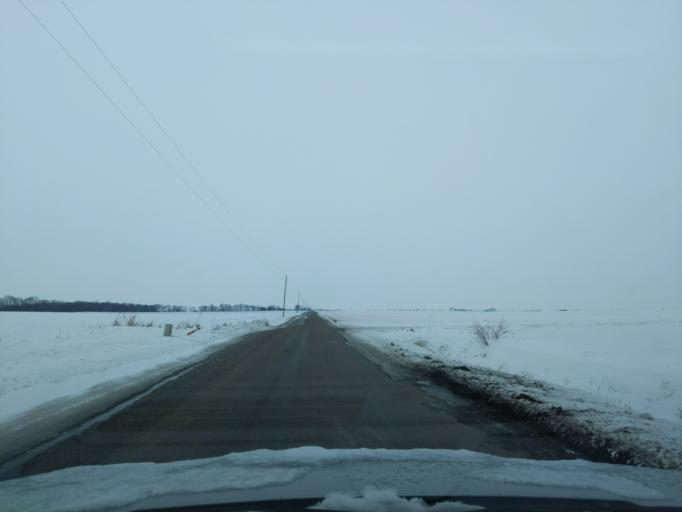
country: US
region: Indiana
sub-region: Benton County
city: Otterbein
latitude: 40.4467
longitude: -87.0925
